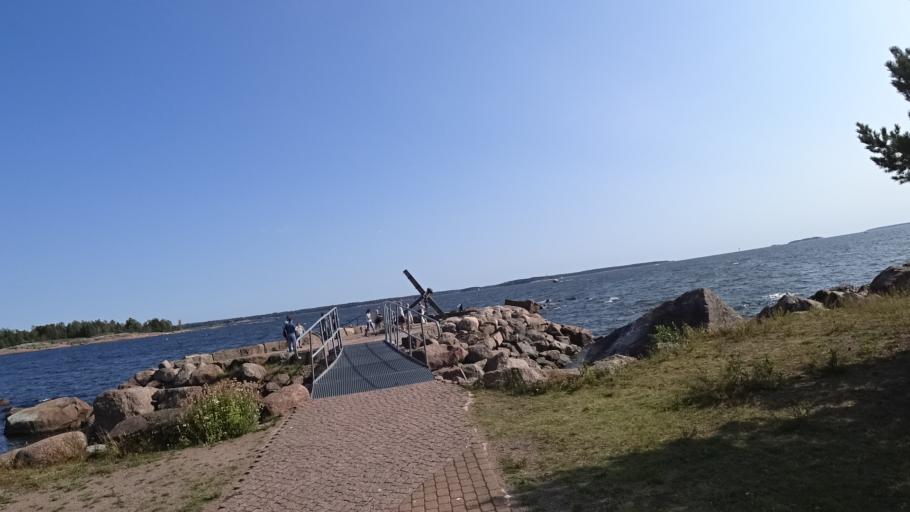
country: FI
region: Kymenlaakso
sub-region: Kotka-Hamina
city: Kotka
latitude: 60.4460
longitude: 26.9419
